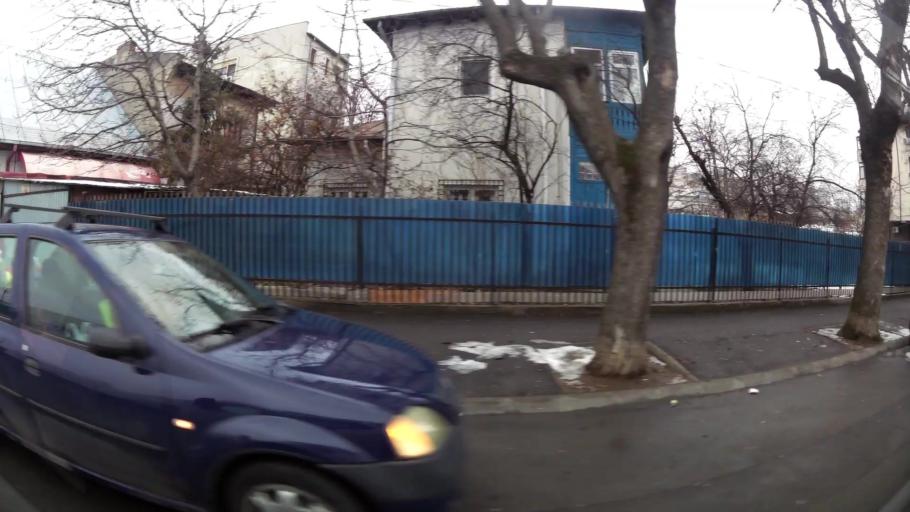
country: RO
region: Ilfov
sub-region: Comuna Chiajna
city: Rosu
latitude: 44.4844
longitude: 26.0345
